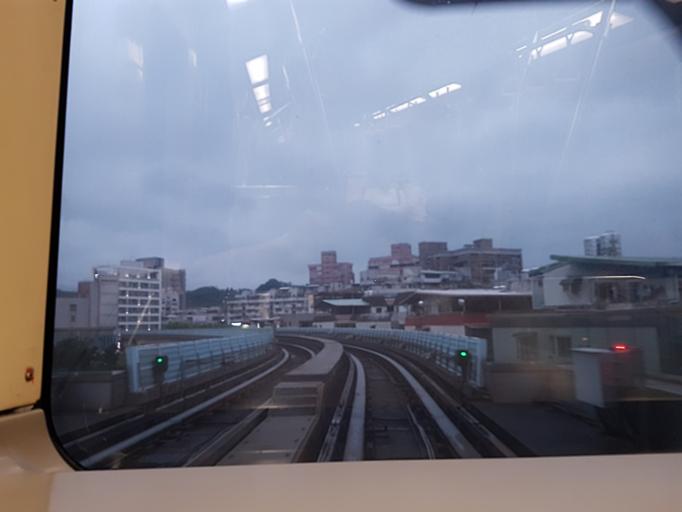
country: TW
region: Taipei
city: Taipei
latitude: 25.0678
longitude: 121.6118
